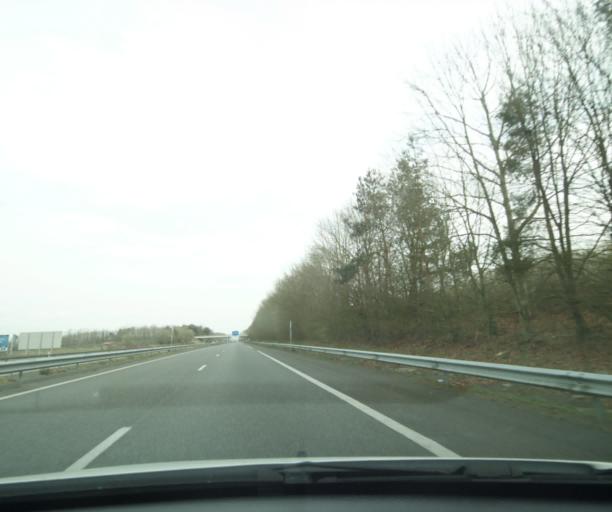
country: FR
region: Aquitaine
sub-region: Departement des Landes
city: Peyrehorade
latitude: 43.5142
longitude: -1.1138
